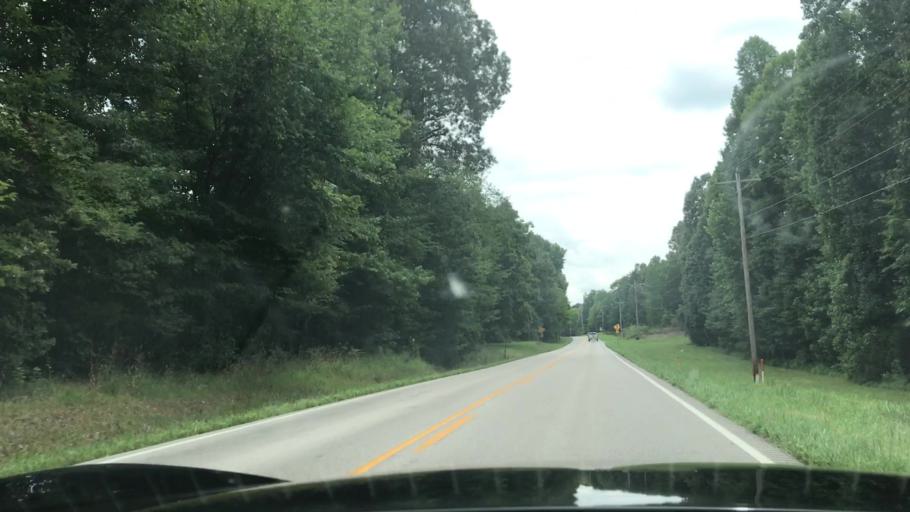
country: US
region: Kentucky
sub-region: Butler County
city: Morgantown
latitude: 37.1884
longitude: -86.8786
